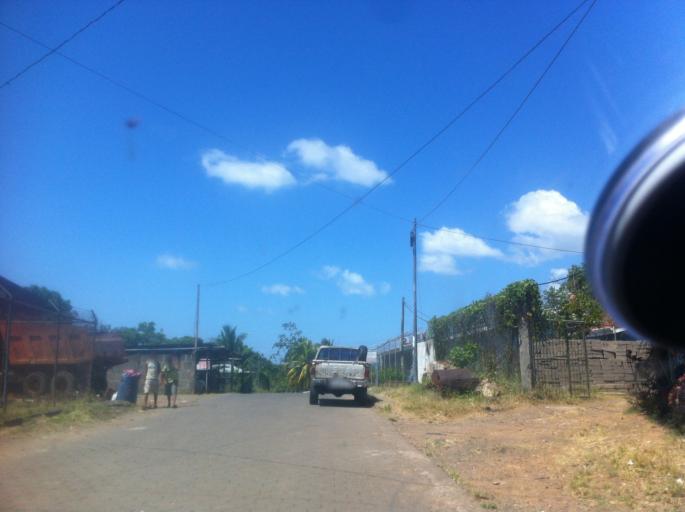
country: NI
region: Rio San Juan
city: San Carlos
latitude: 11.1327
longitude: -84.7726
